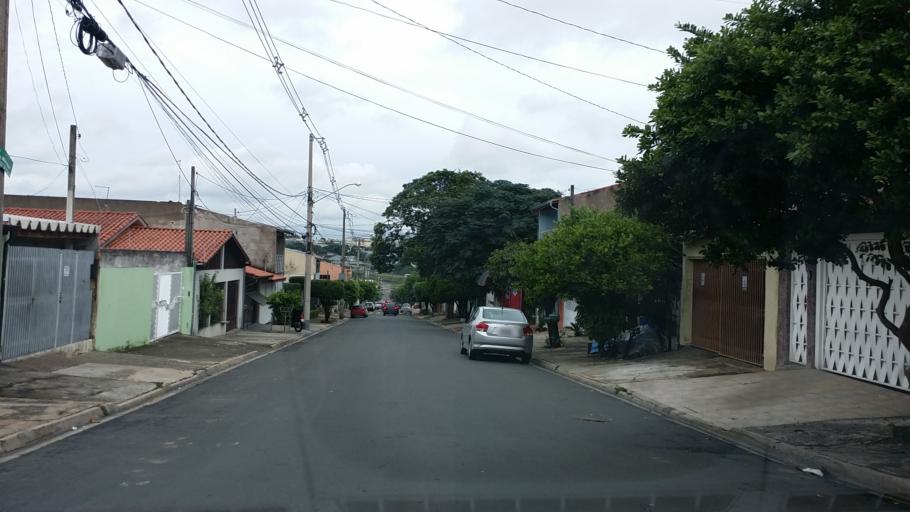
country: BR
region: Sao Paulo
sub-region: Indaiatuba
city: Indaiatuba
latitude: -23.1262
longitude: -47.2383
